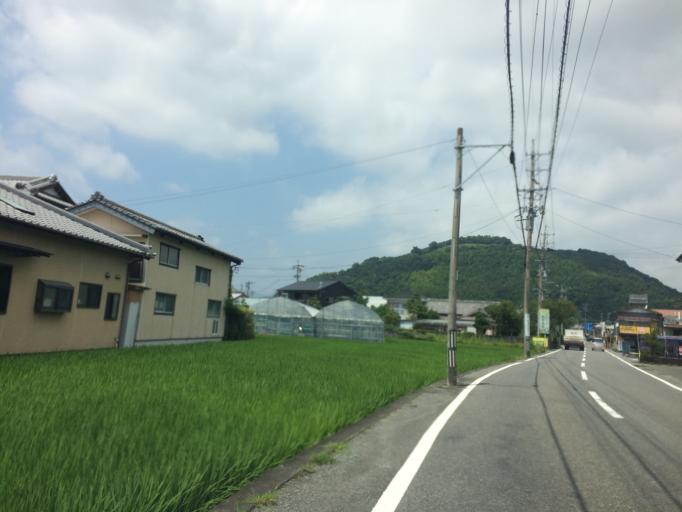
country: JP
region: Shizuoka
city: Shimada
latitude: 34.8340
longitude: 138.2017
